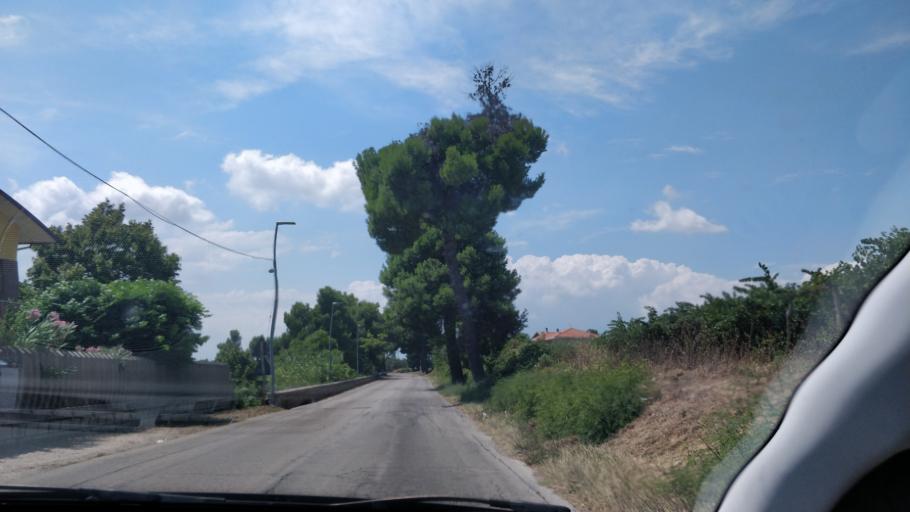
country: IT
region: Abruzzo
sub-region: Provincia di Chieti
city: Torrevecchia
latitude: 42.4081
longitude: 14.2239
